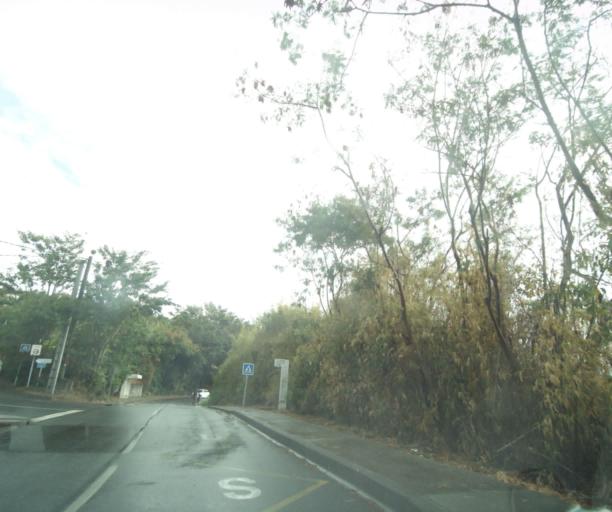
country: RE
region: Reunion
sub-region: Reunion
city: Saint-Paul
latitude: -21.0067
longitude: 55.3217
